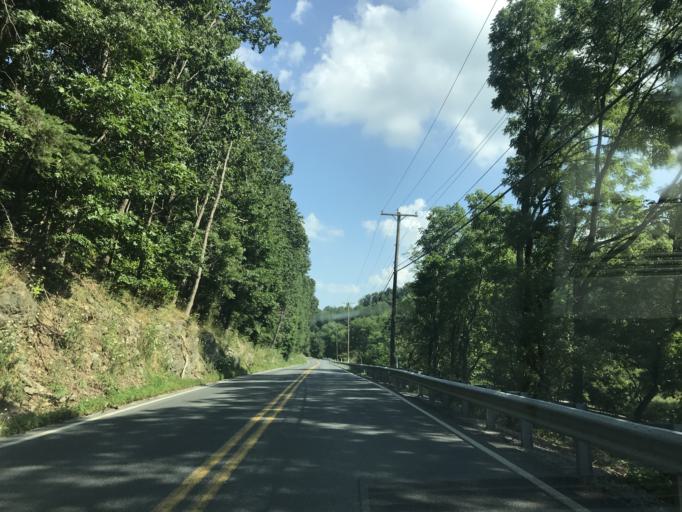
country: US
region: Pennsylvania
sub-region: York County
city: Glen Rock
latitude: 39.7644
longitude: -76.8219
